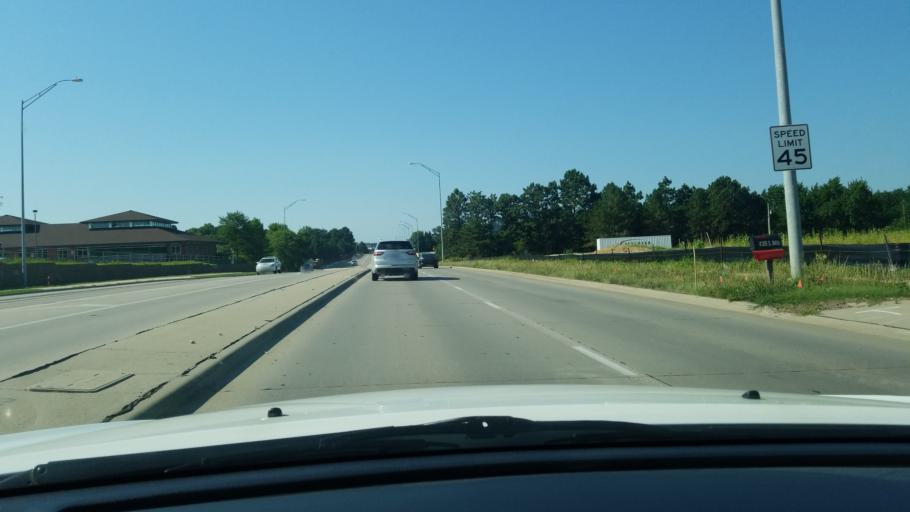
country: US
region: Nebraska
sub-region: Lancaster County
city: Lincoln
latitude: 40.7689
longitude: -96.6062
